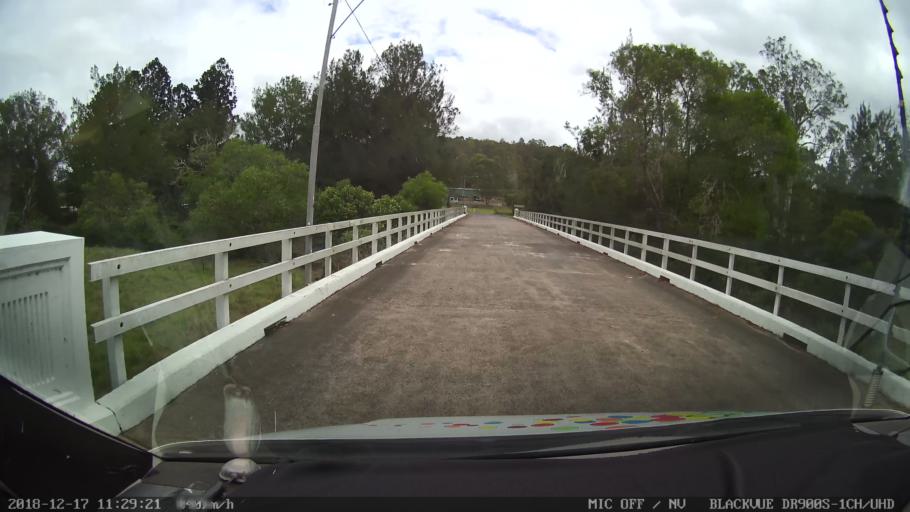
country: AU
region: New South Wales
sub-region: Kyogle
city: Kyogle
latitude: -28.7396
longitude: 152.6292
